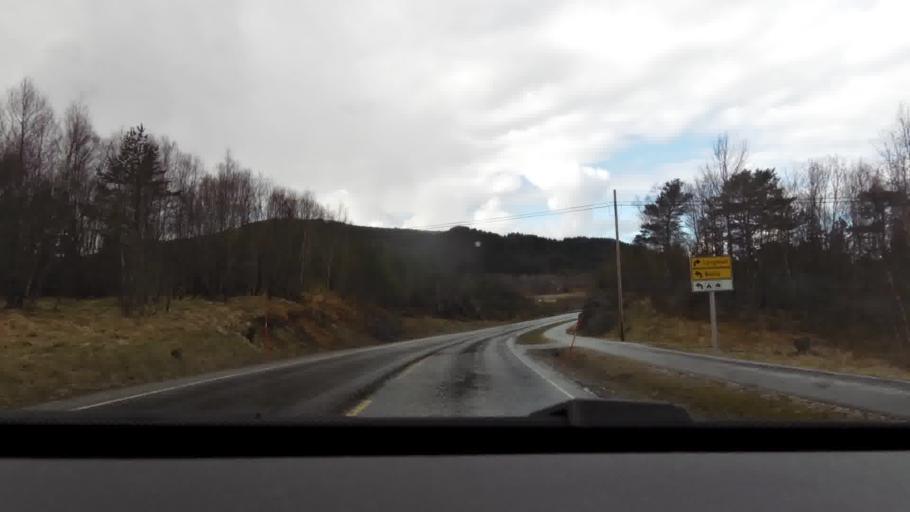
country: NO
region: More og Romsdal
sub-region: Eide
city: Eide
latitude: 62.9575
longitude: 7.3655
